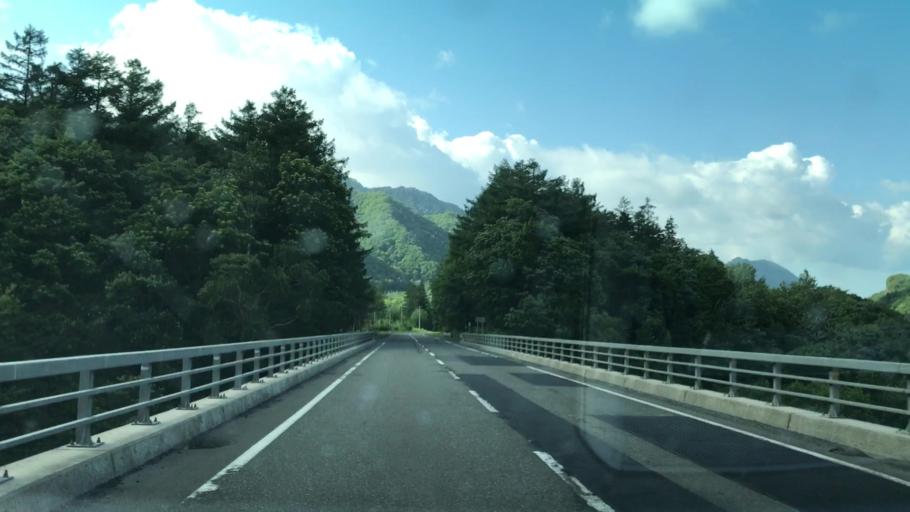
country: JP
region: Hokkaido
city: Shizunai-furukawacho
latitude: 42.8221
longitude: 142.4183
